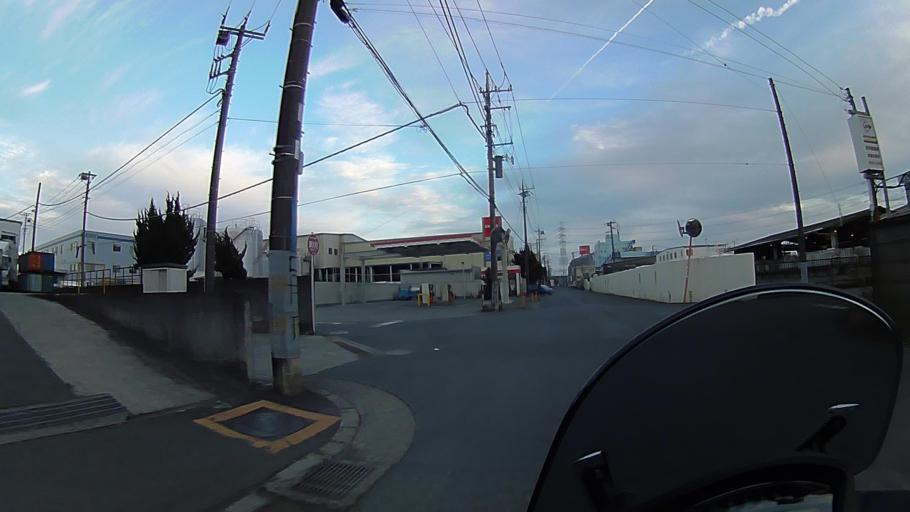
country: JP
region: Kanagawa
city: Minami-rinkan
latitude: 35.4249
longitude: 139.4246
